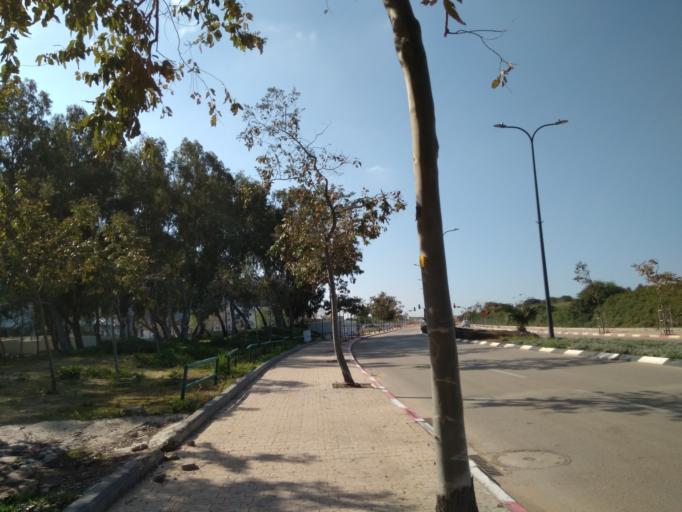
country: IL
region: Tel Aviv
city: Herzliya Pituah
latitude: 32.1611
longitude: 34.8056
